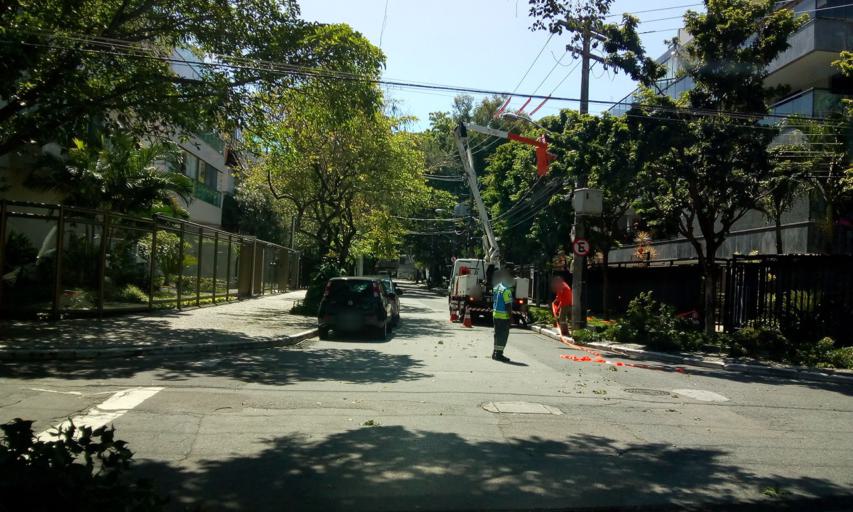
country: BR
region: Rio de Janeiro
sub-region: Rio De Janeiro
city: Rio de Janeiro
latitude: -23.0105
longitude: -43.3199
